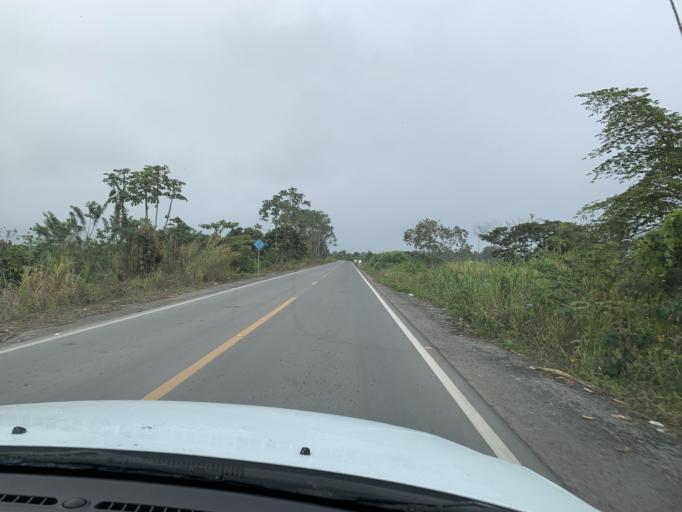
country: EC
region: Guayas
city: Coronel Marcelino Mariduena
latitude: -2.3013
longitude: -79.5025
